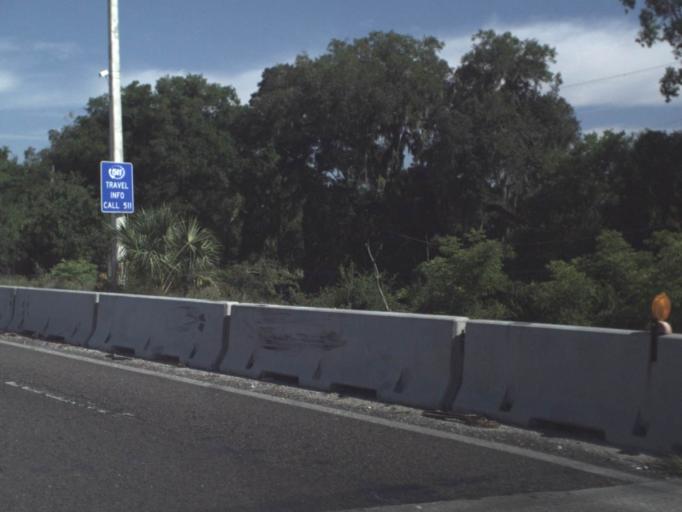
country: US
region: Florida
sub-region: Saint Johns County
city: Fruit Cove
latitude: 30.1842
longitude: -81.6352
